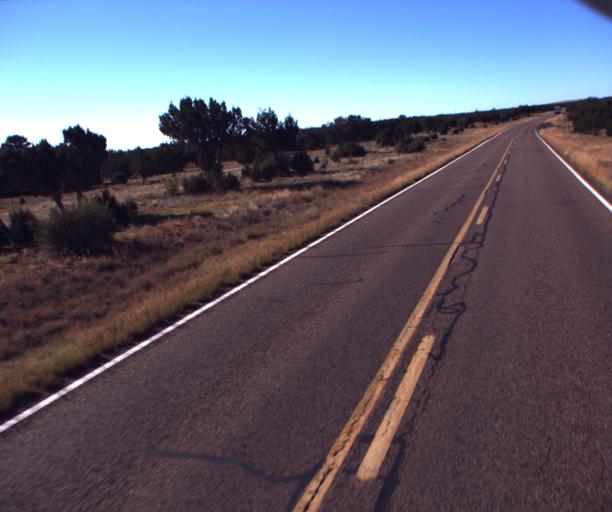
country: US
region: Arizona
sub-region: Navajo County
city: Heber-Overgaard
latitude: 34.4927
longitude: -110.4568
